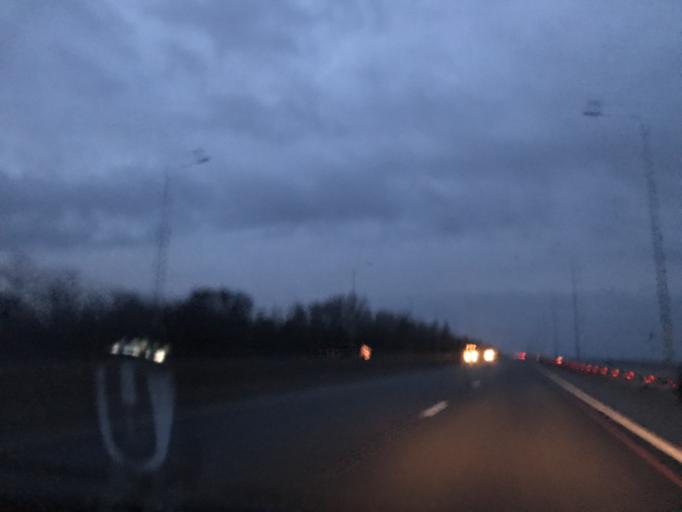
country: RU
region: Rostov
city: Samarskoye
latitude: 46.9951
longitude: 39.7282
